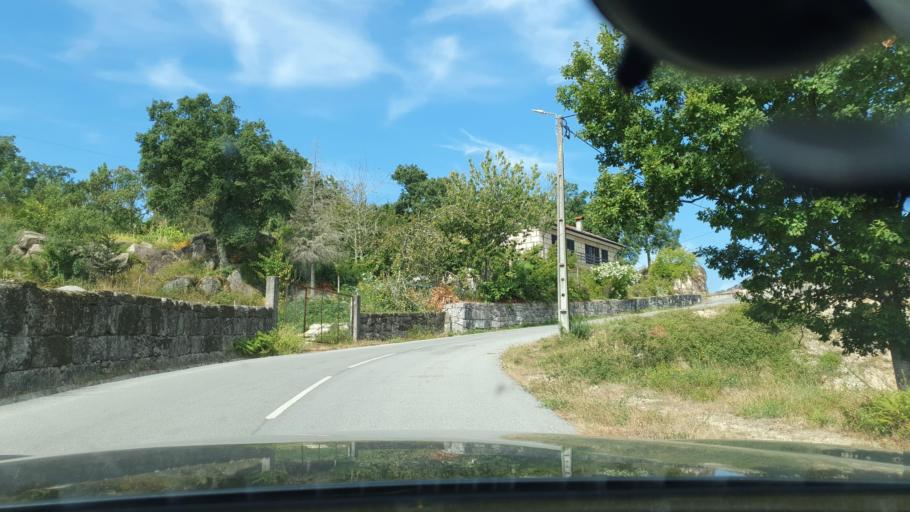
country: PT
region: Braga
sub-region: Vieira do Minho
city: Vieira do Minho
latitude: 41.6999
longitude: -8.0856
